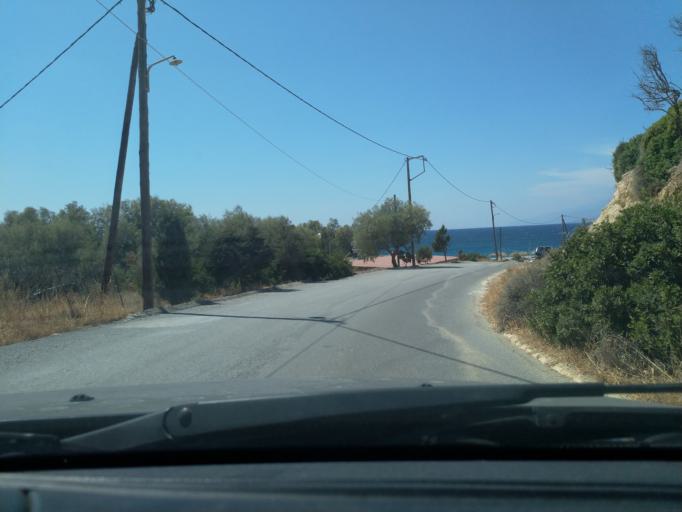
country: GR
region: Crete
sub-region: Nomos Rethymnis
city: Agia Galini
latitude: 35.1192
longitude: 24.5481
